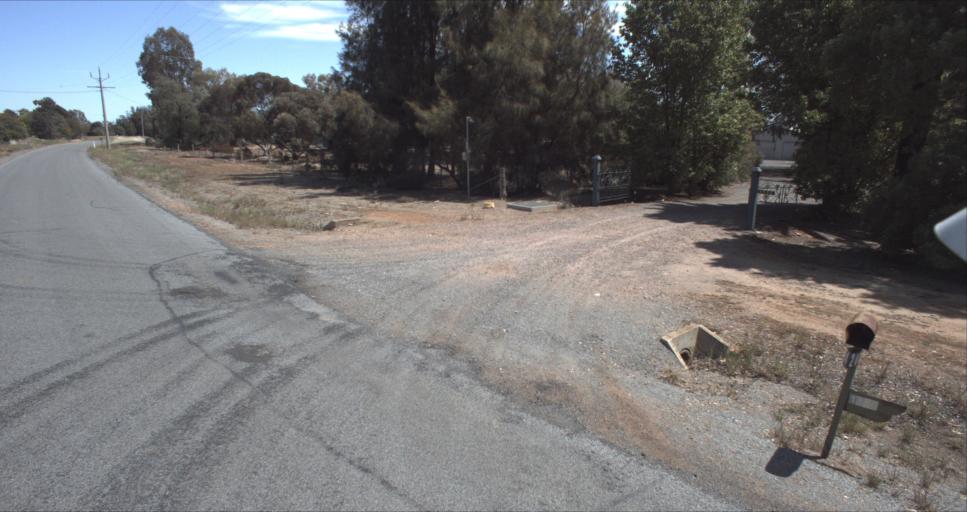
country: AU
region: New South Wales
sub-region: Leeton
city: Leeton
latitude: -34.5715
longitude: 146.4368
